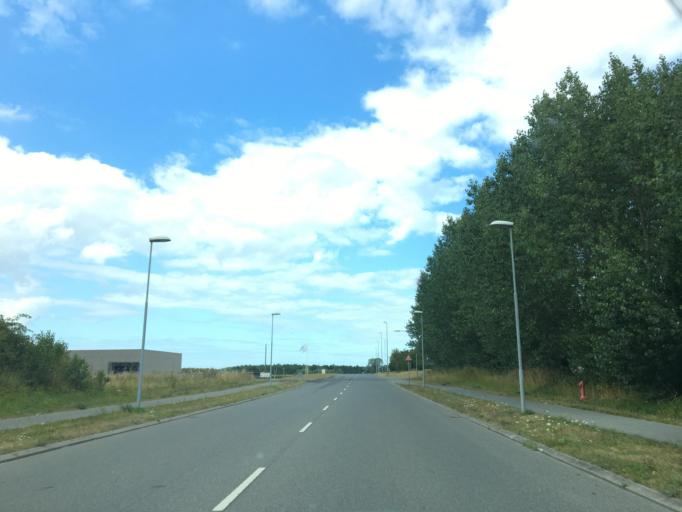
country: DK
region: South Denmark
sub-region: Nyborg Kommune
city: Nyborg
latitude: 55.3152
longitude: 10.7478
